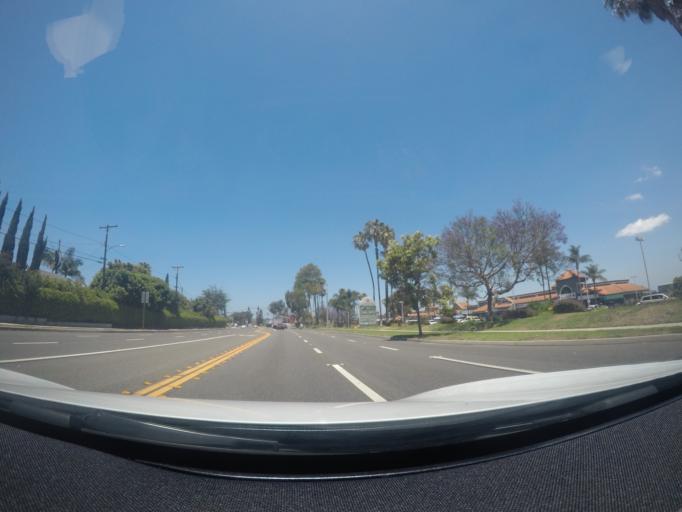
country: US
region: California
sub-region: Los Angeles County
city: Rolling Hills Estates
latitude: 33.8027
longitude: -118.3466
